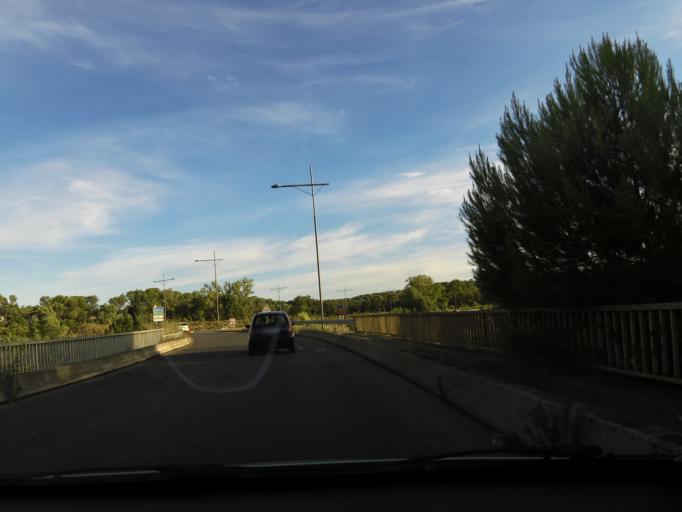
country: FR
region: Languedoc-Roussillon
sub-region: Departement de l'Herault
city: Clapiers
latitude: 43.6543
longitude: 3.8719
